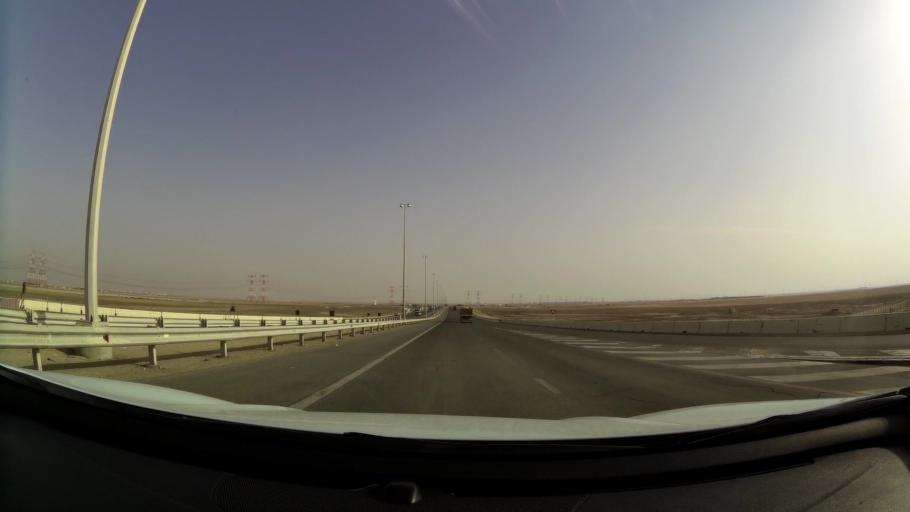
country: AE
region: Abu Dhabi
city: Abu Dhabi
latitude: 24.2109
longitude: 54.4161
